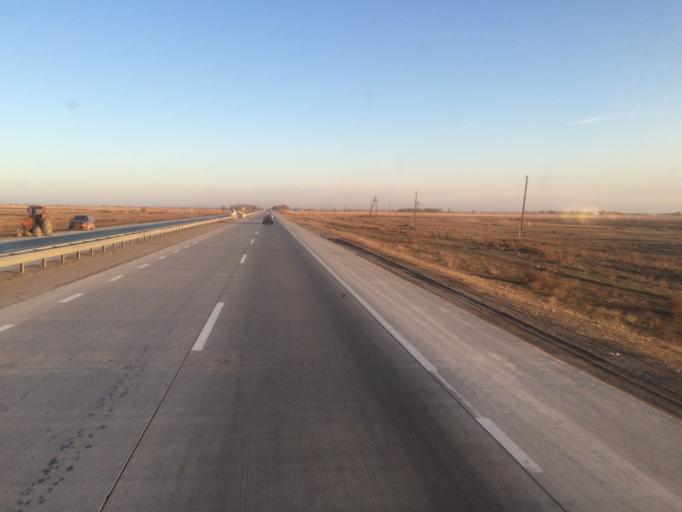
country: KZ
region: Ongtustik Qazaqstan
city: Turkestan
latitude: 43.2358
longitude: 68.4284
